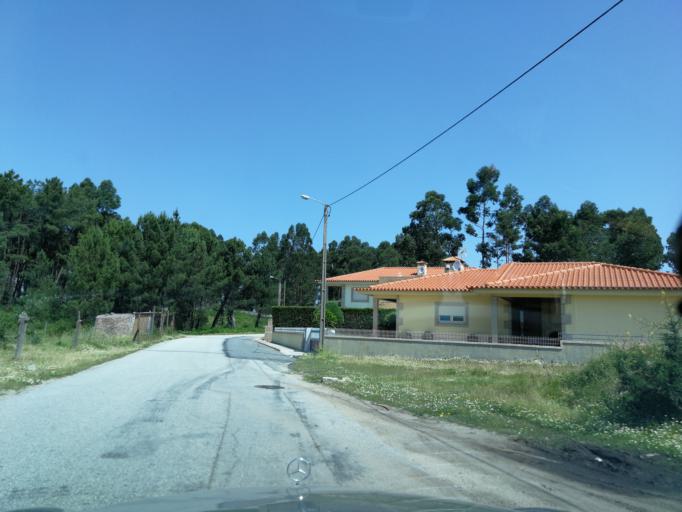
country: PT
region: Braga
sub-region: Braga
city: Adaufe
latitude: 41.5566
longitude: -8.3490
